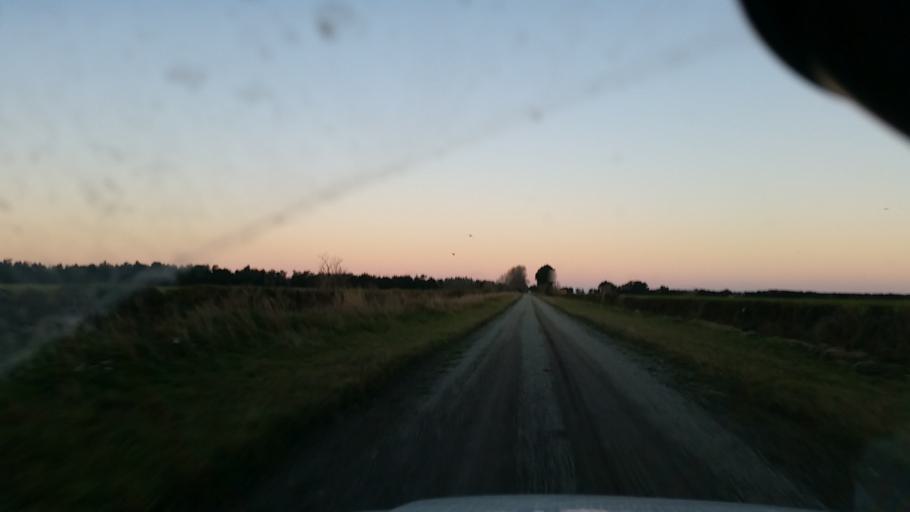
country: NZ
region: Canterbury
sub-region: Ashburton District
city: Tinwald
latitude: -44.0879
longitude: 171.6685
